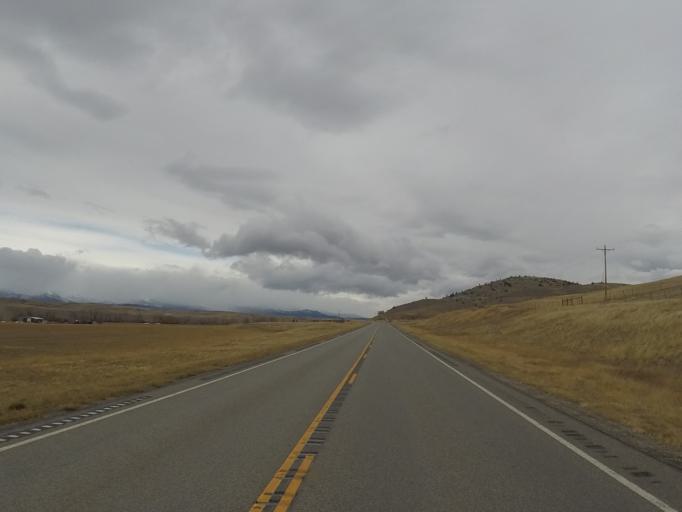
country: US
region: Montana
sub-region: Sweet Grass County
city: Big Timber
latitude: 45.8723
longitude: -109.9472
